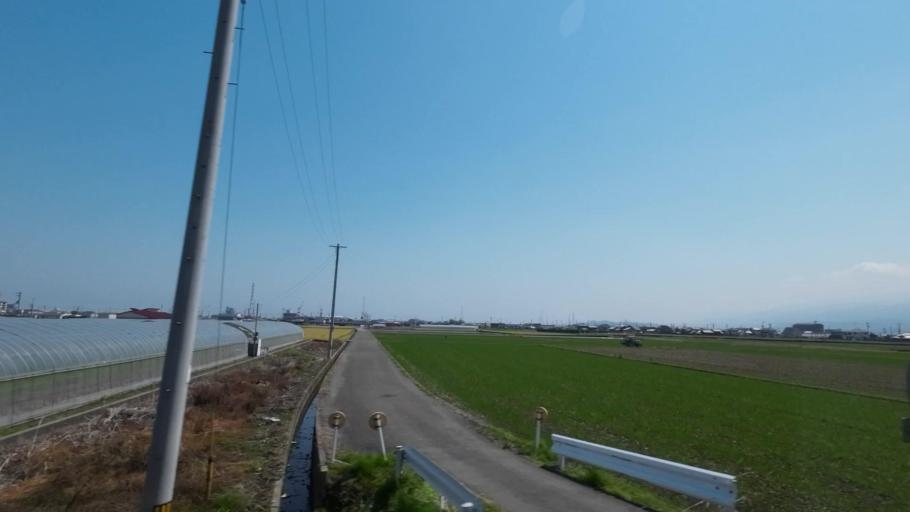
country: JP
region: Ehime
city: Saijo
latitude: 33.9157
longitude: 133.0980
